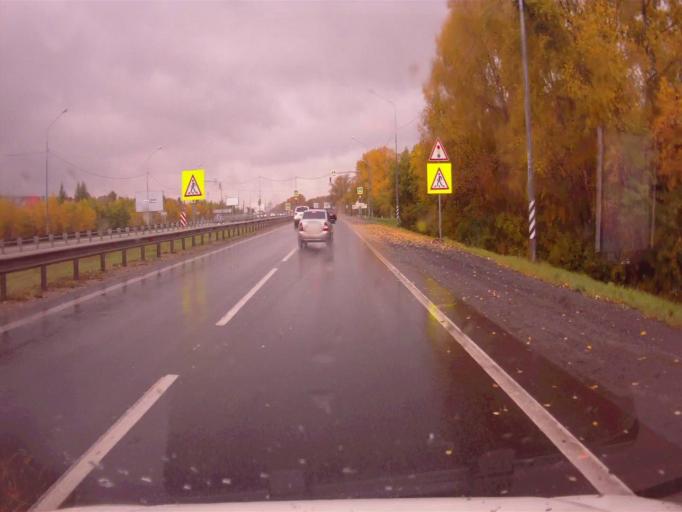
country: RU
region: Chelyabinsk
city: Dolgoderevenskoye
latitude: 55.2821
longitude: 61.3431
